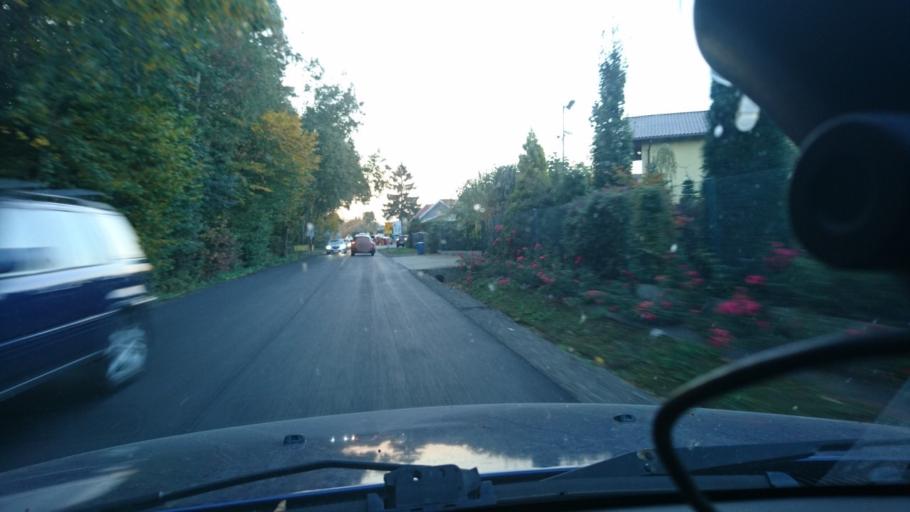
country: PL
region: Silesian Voivodeship
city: Janowice
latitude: 49.8513
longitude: 19.1101
